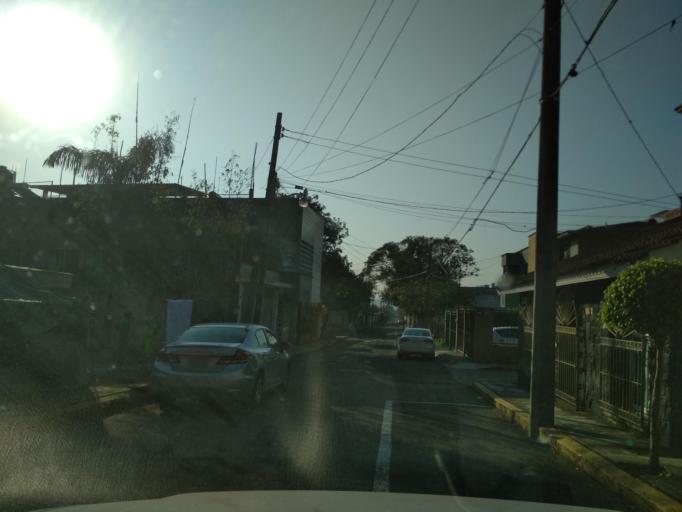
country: MX
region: Veracruz
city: Ixtac Zoquitlan
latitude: 18.8617
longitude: -97.0790
